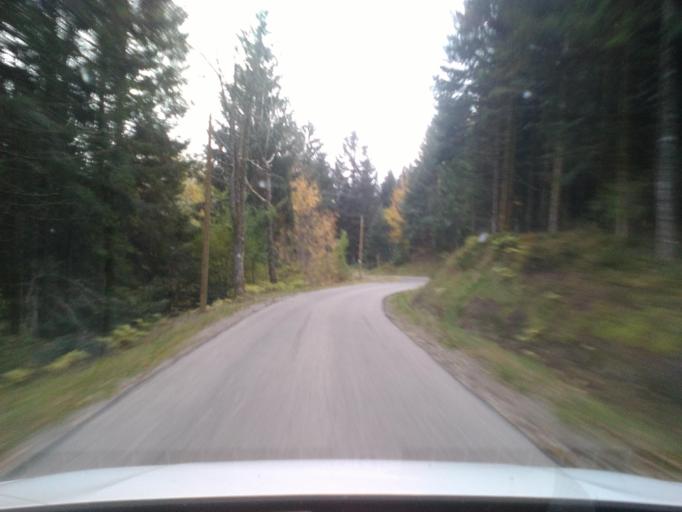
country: FR
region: Lorraine
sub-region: Departement des Vosges
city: Gerardmer
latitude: 48.0837
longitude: 6.8555
